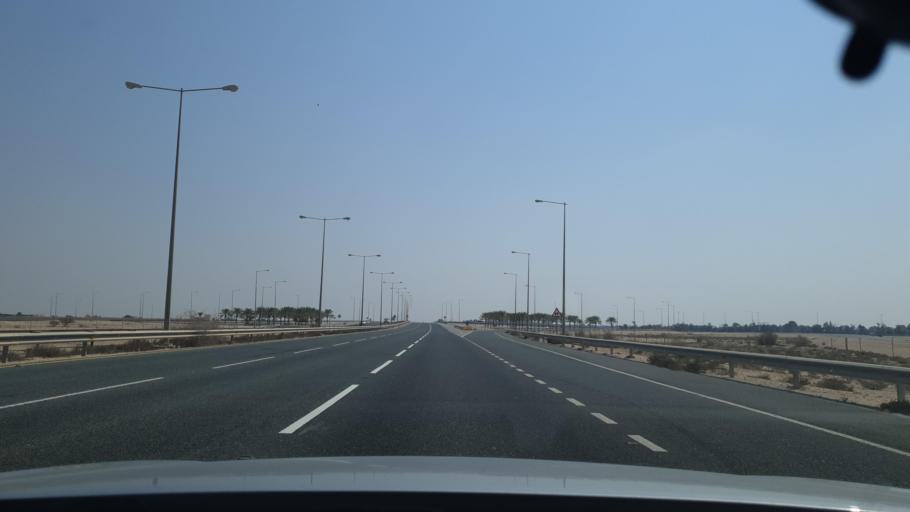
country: QA
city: Al Ghuwayriyah
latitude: 25.7895
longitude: 51.3925
